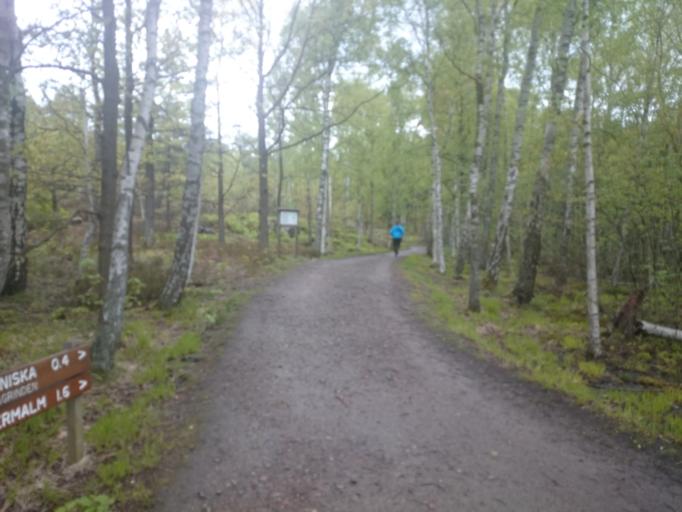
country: SE
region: Vaestra Goetaland
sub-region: Goteborg
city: Goeteborg
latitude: 57.6744
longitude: 11.9547
